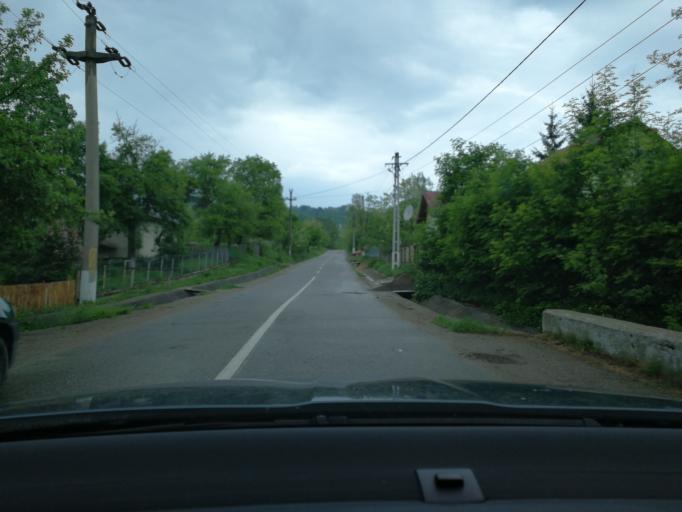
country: RO
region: Prahova
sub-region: Comuna Brebu
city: Pietriceaua
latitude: 45.2051
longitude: 25.8271
